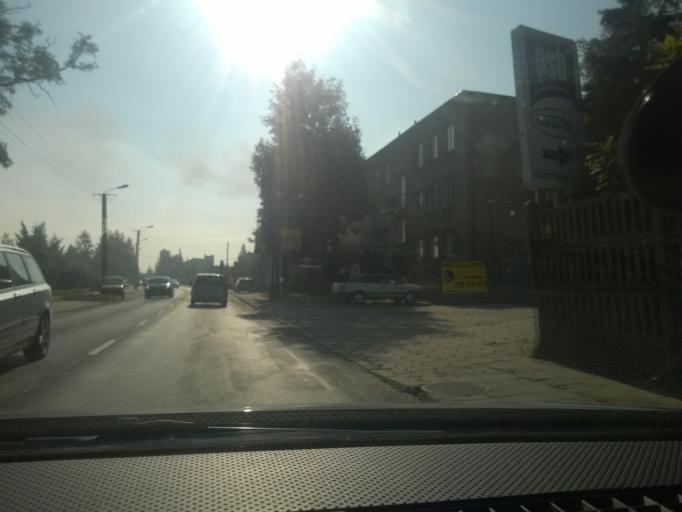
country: PL
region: Greater Poland Voivodeship
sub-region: Kalisz
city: Kalisz
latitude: 51.7444
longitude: 18.0964
